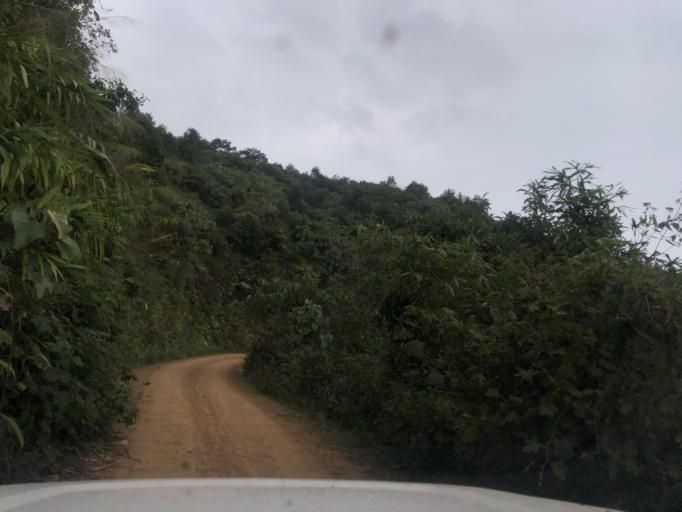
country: LA
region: Phongsali
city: Khoa
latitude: 21.2628
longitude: 102.5890
